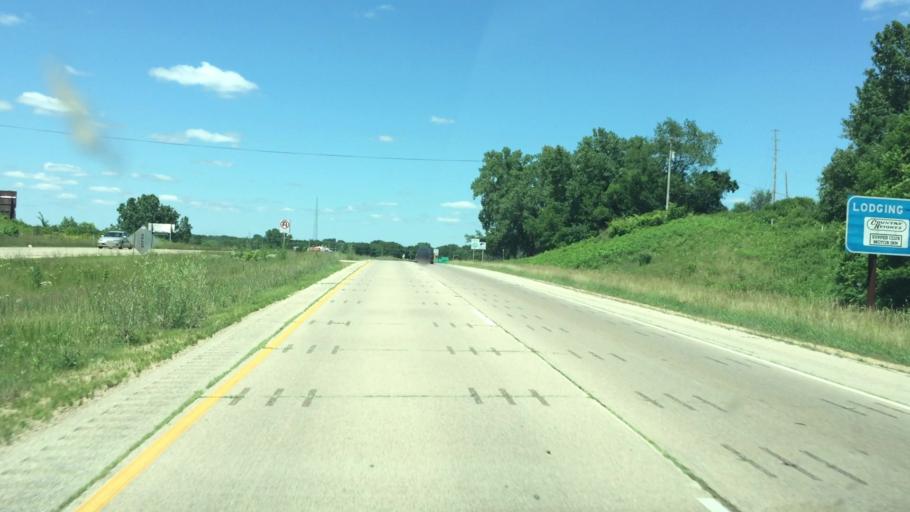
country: US
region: Illinois
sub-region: Jo Daviess County
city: East Dubuque
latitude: 42.5277
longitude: -90.6136
